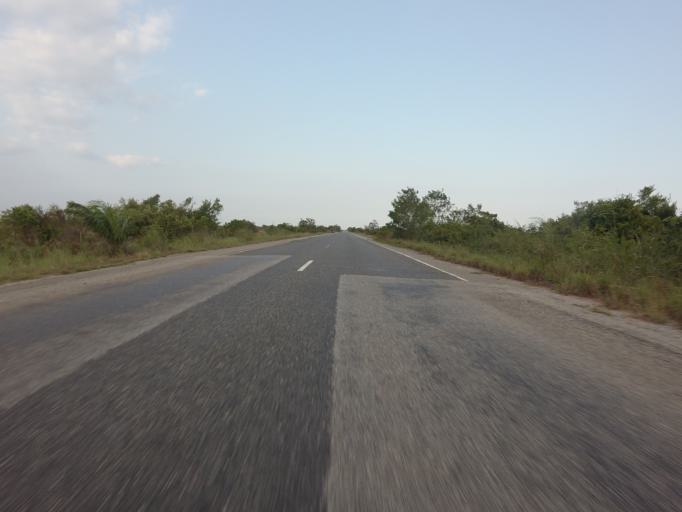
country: GH
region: Volta
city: Anloga
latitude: 6.0826
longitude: 0.5673
